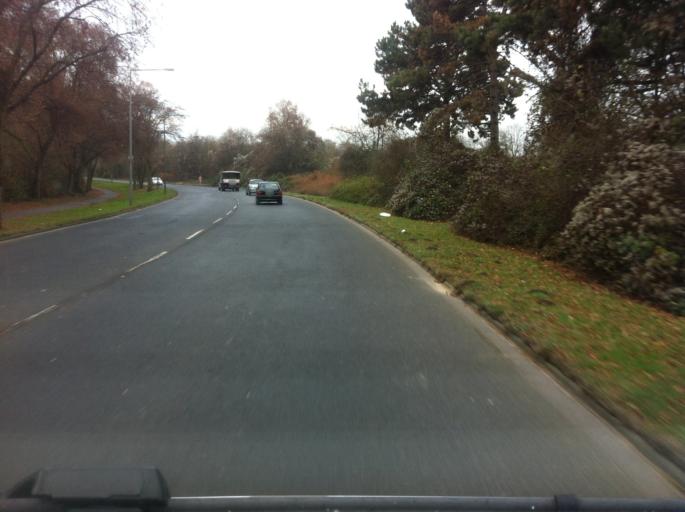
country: DE
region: North Rhine-Westphalia
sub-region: Regierungsbezirk Koln
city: Bilderstoeckchen
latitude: 50.9759
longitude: 6.9089
